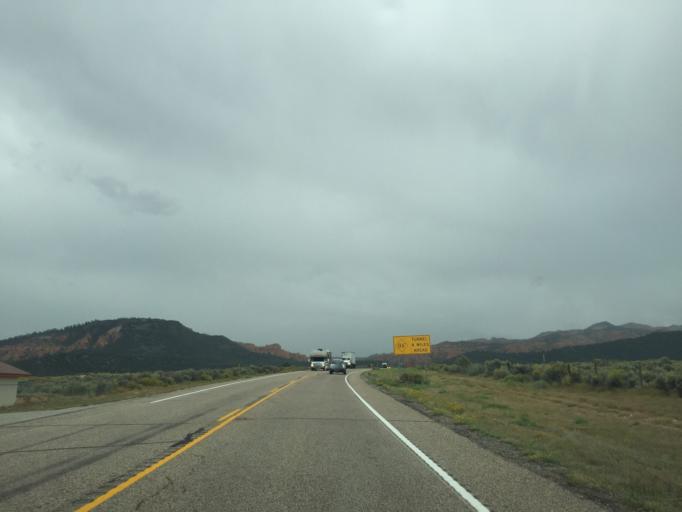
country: US
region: Utah
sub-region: Garfield County
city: Panguitch
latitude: 37.7486
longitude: -112.3611
